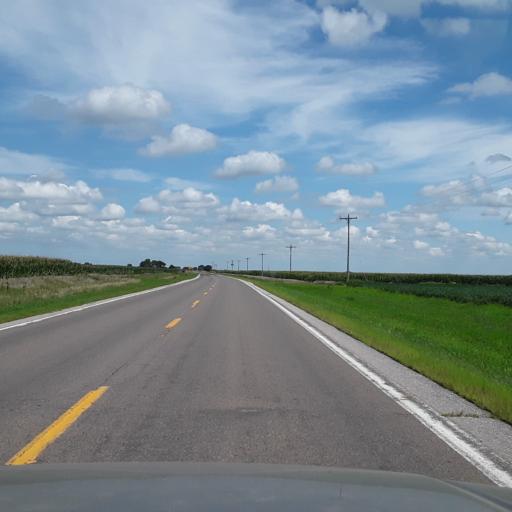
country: US
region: Nebraska
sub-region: Polk County
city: Osceola
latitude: 41.0675
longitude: -97.4061
